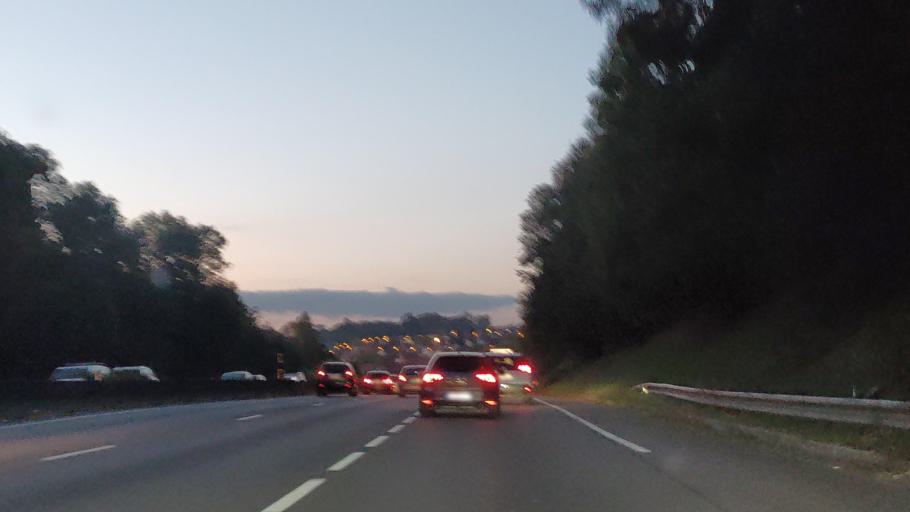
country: FR
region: Ile-de-France
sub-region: Departement de l'Essonne
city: Savigny-sur-Orge
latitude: 48.6756
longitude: 2.3468
